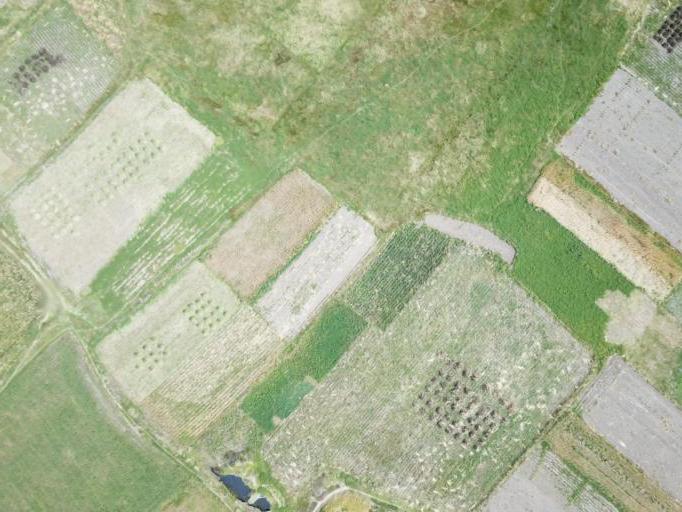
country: BO
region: La Paz
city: Achacachi
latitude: -16.0525
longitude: -68.8187
